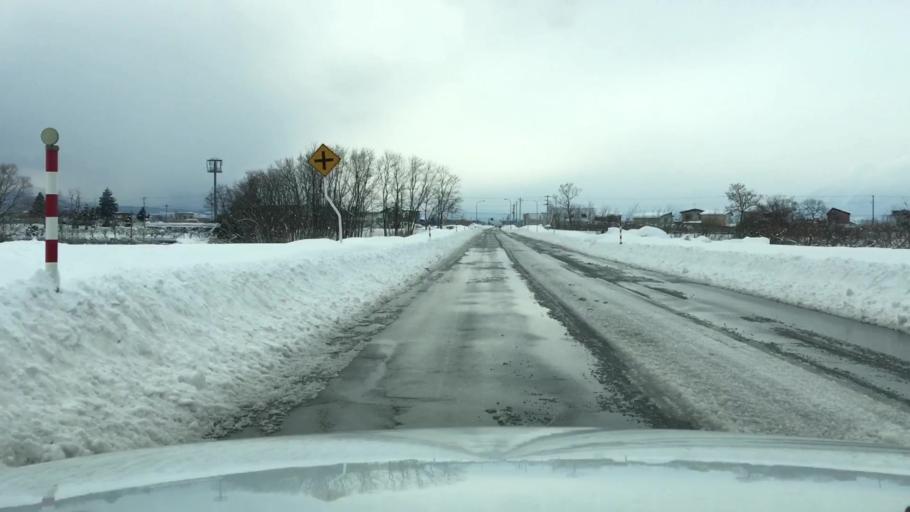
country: JP
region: Aomori
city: Kuroishi
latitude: 40.5931
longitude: 140.5940
